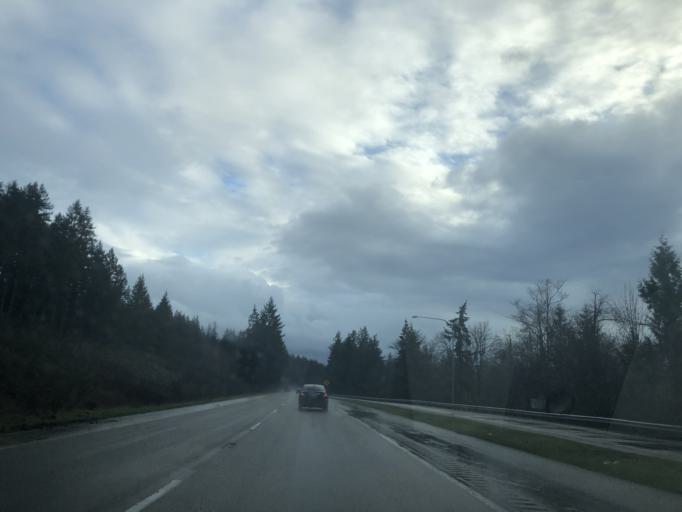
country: US
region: Washington
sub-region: Kitsap County
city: Burley
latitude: 47.4233
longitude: -122.6239
